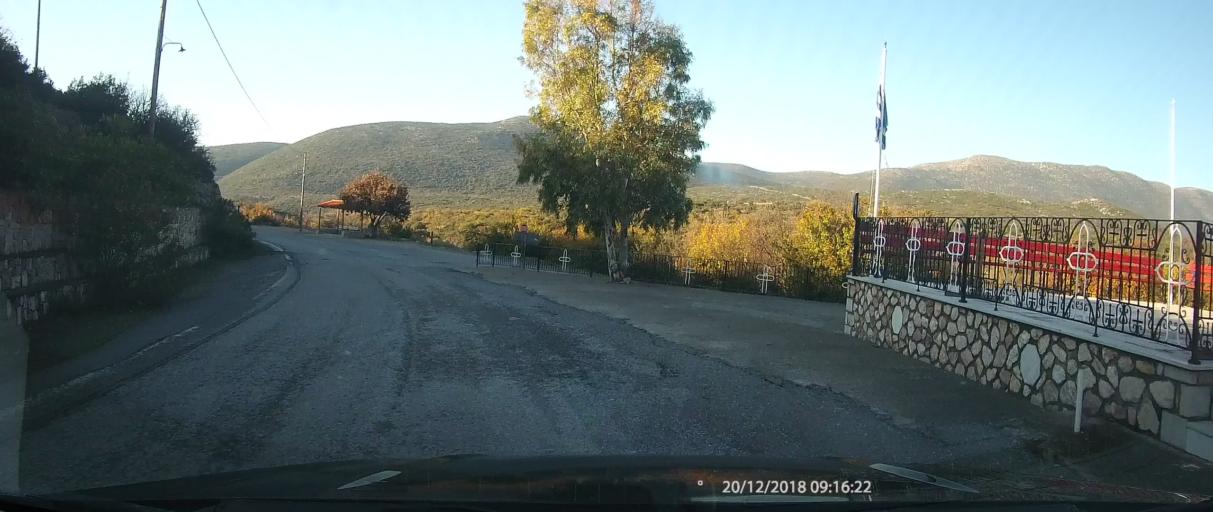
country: GR
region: Peloponnese
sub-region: Nomos Lakonias
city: Sykea
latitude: 36.9021
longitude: 22.9697
